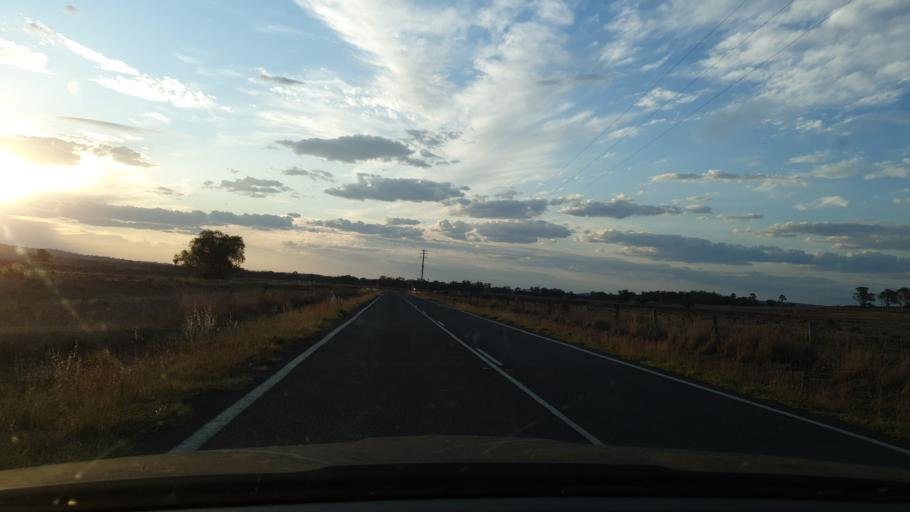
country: AU
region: Queensland
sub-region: Southern Downs
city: Warwick
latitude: -28.1824
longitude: 151.9825
